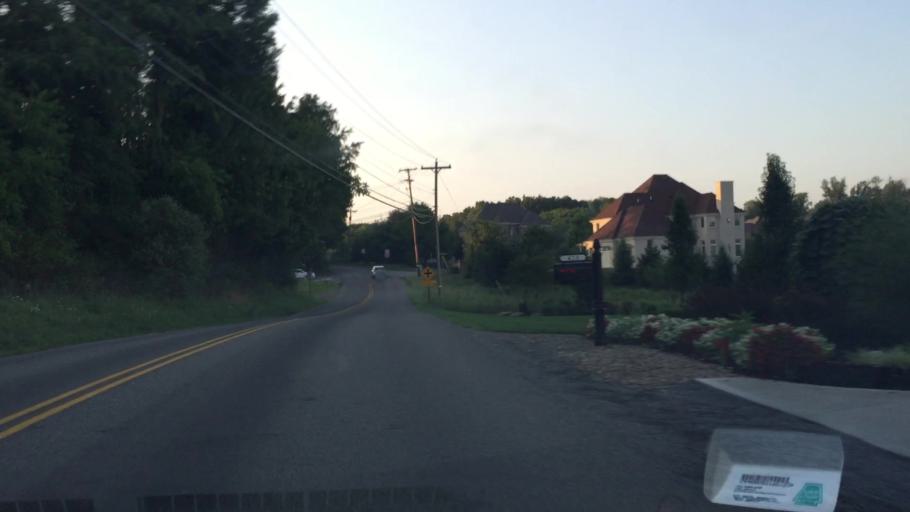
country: US
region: Pennsylvania
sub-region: Butler County
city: Seven Fields
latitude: 40.7041
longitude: -80.0515
